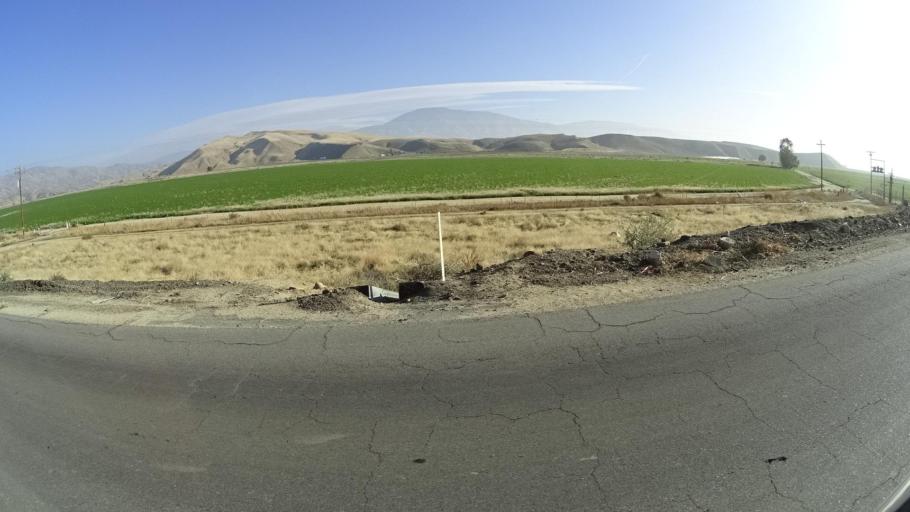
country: US
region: California
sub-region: Kern County
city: Arvin
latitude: 35.3269
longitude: -118.7728
